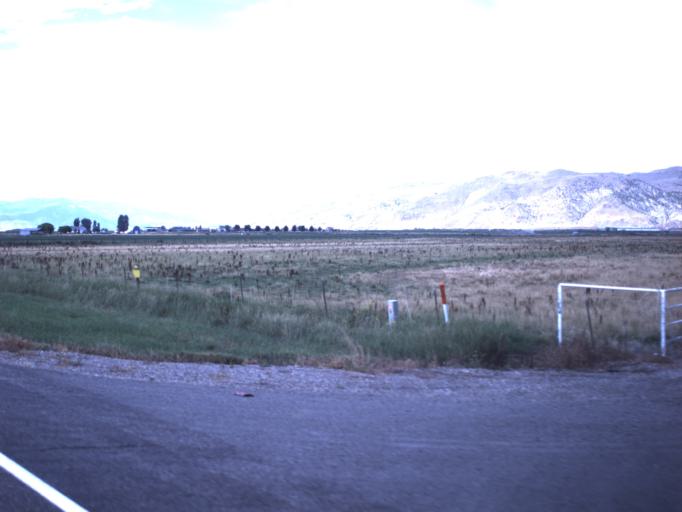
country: US
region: Utah
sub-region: Sevier County
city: Richfield
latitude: 38.7167
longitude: -112.1037
